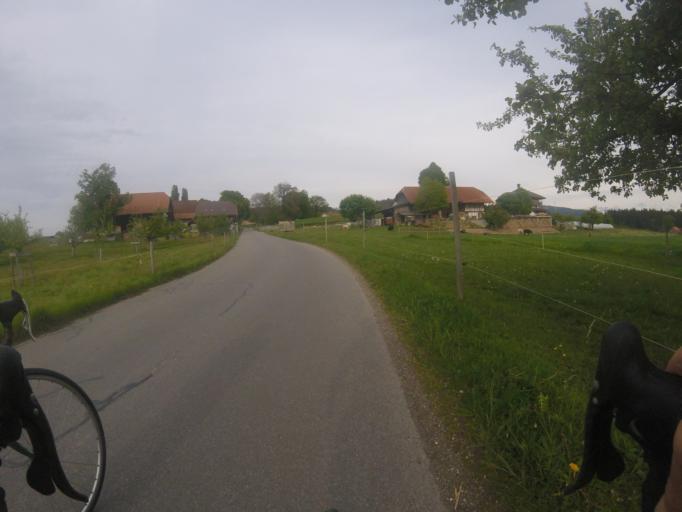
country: CH
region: Bern
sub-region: Bern-Mittelland District
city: Niederwichtrach
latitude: 46.8403
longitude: 7.5913
